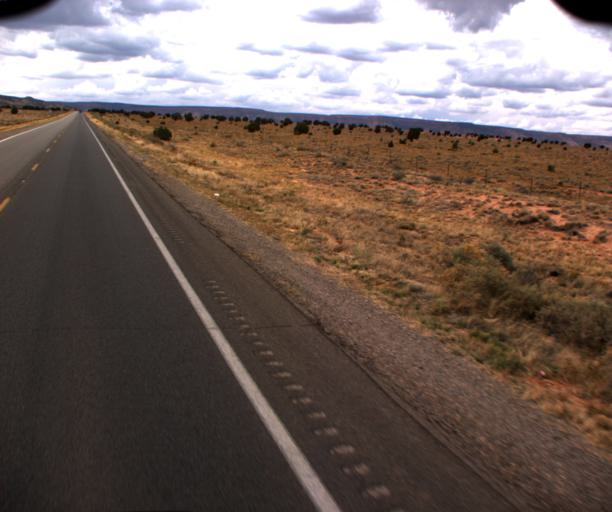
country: US
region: Arizona
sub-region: Navajo County
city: Kayenta
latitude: 36.7020
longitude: -110.2849
